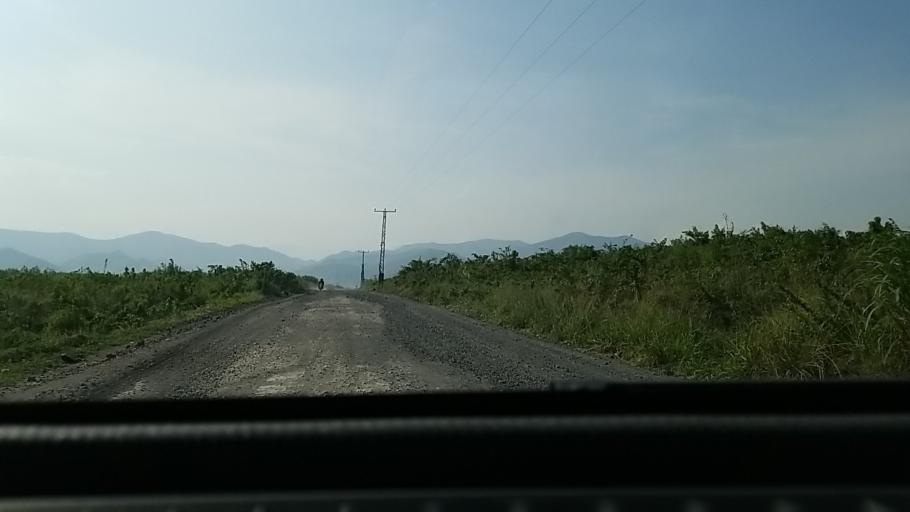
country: CD
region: Nord Kivu
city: Sake
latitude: -1.5838
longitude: 29.0845
